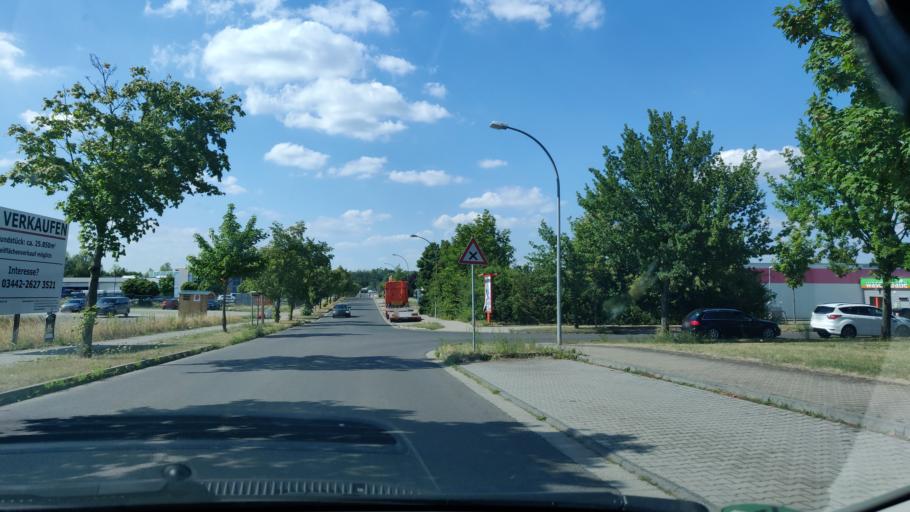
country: DE
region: Saxony
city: Borna
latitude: 51.1117
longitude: 12.4881
